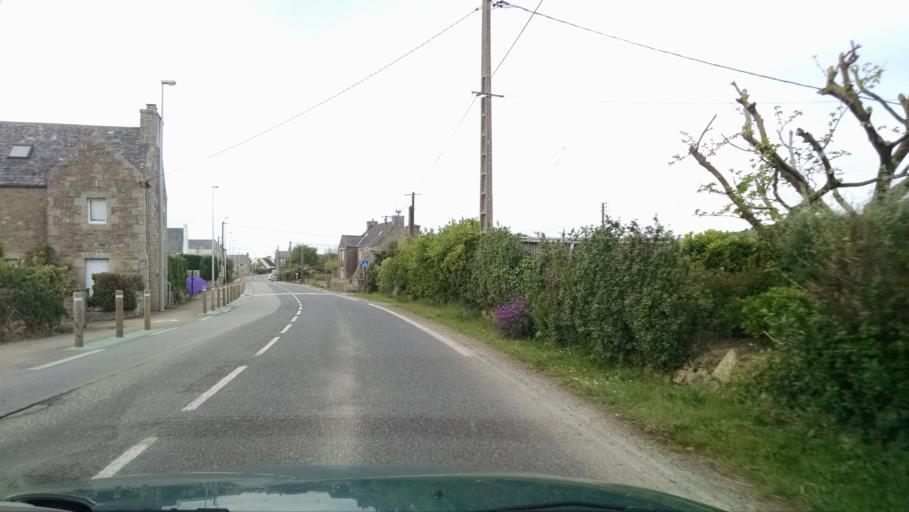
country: FR
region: Brittany
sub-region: Departement du Finistere
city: Saint-Pol-de-Leon
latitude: 48.6983
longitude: -3.9868
